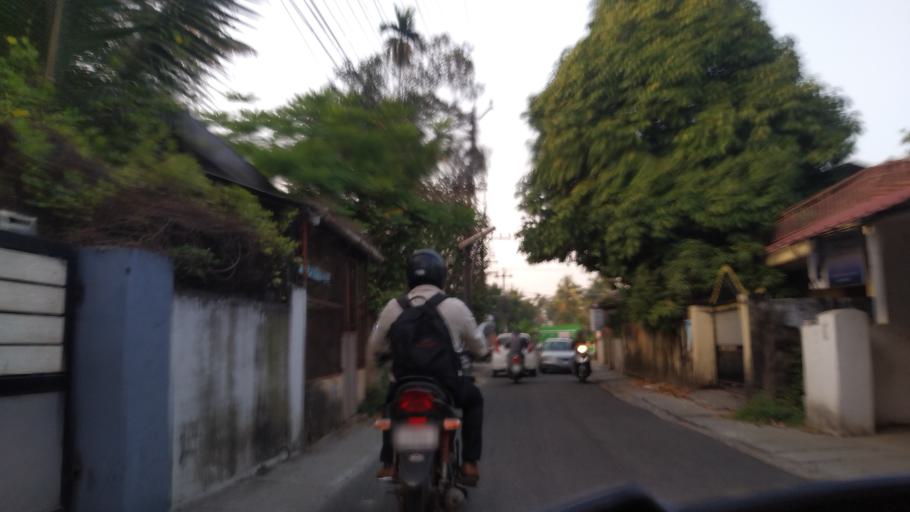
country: IN
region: Kerala
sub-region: Ernakulam
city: Elur
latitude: 10.0328
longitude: 76.2756
